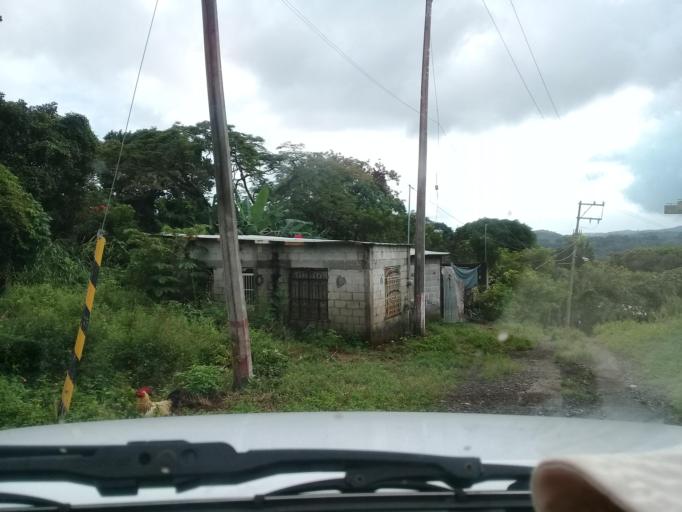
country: MX
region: Veracruz
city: Catemaco
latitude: 18.4285
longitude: -95.1254
